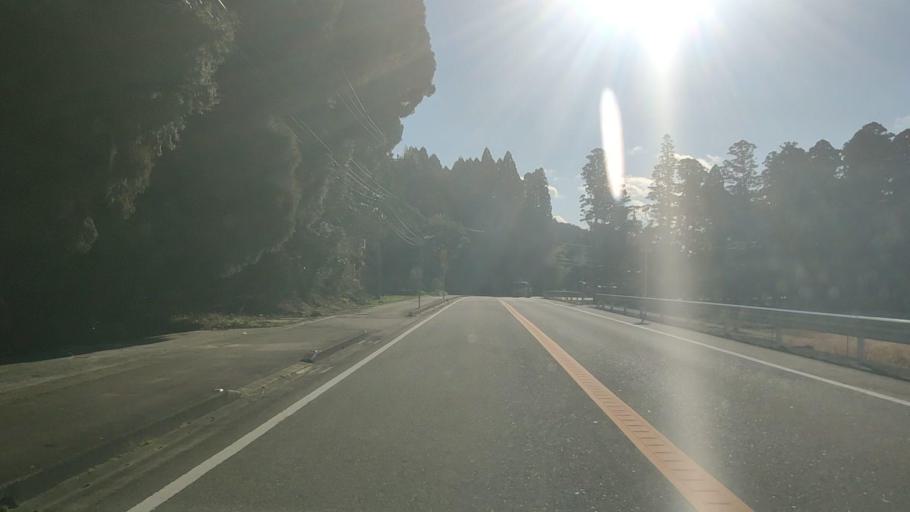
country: JP
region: Fukuoka
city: Maebaru-chuo
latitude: 33.4458
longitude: 130.2713
